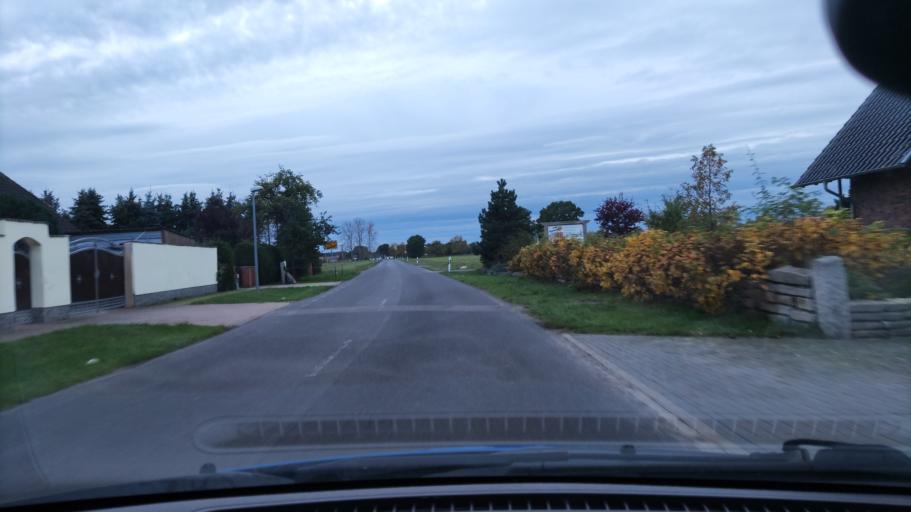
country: DE
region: Saxony-Anhalt
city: Luftkurort Arendsee
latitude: 52.9010
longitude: 11.4669
